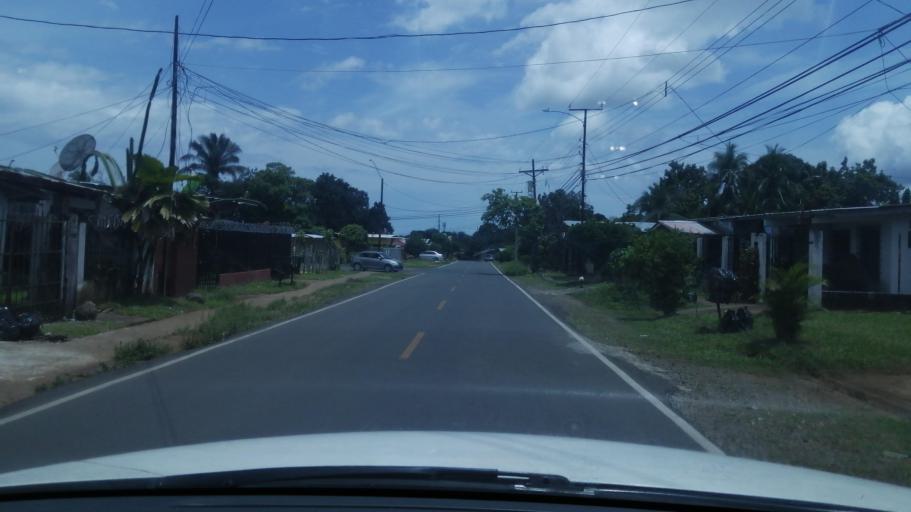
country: PA
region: Chiriqui
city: David
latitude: 8.4171
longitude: -82.4270
